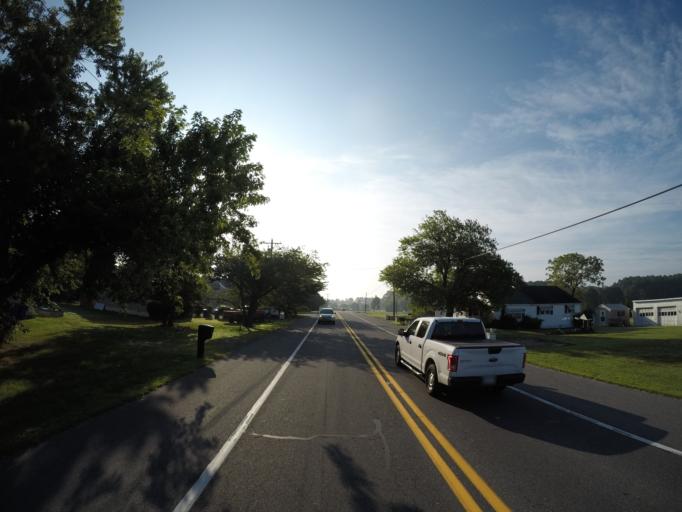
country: US
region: Delaware
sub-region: Sussex County
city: Millsboro
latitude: 38.5446
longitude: -75.2289
